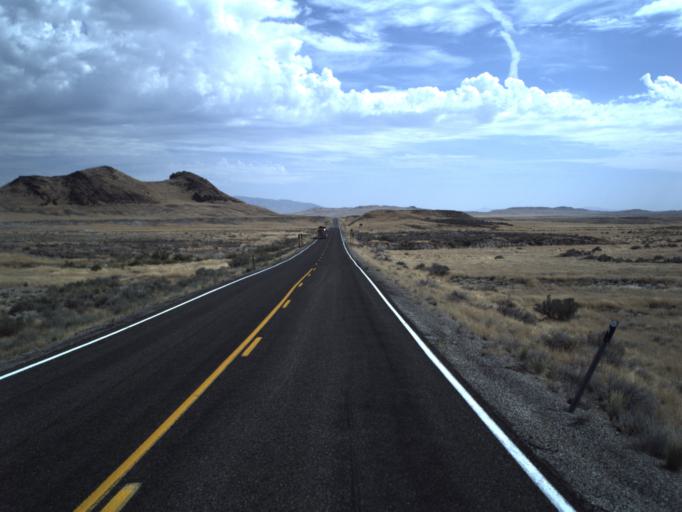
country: US
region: Nevada
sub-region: Elko County
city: West Wendover
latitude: 41.3719
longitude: -114.0266
